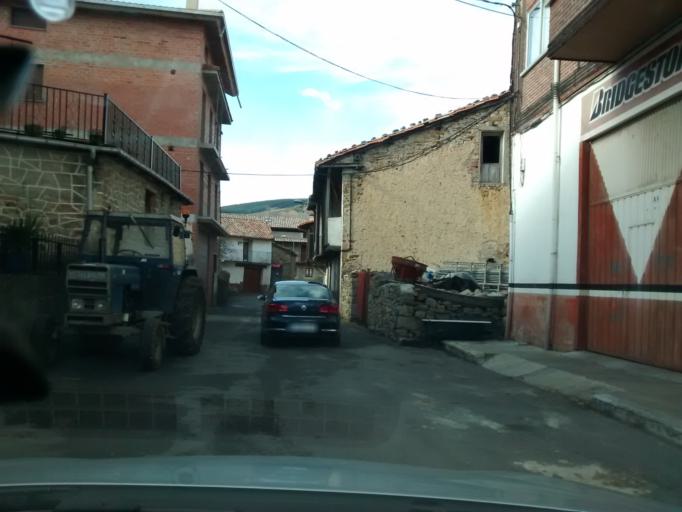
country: ES
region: Castille and Leon
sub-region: Provincia de Burgos
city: Espinosa de los Monteros
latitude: 43.0758
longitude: -3.5463
